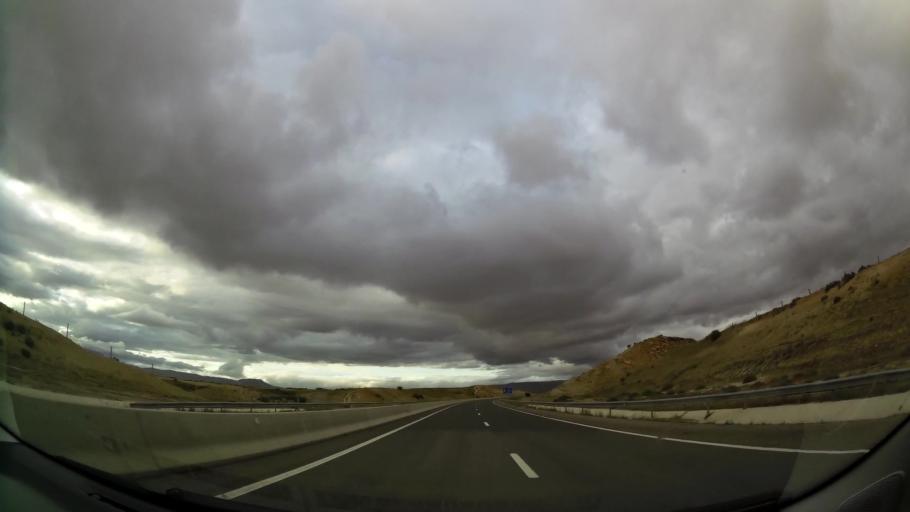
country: MA
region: Taza-Al Hoceima-Taounate
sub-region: Taza
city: Taza
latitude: 34.2966
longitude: -3.7780
